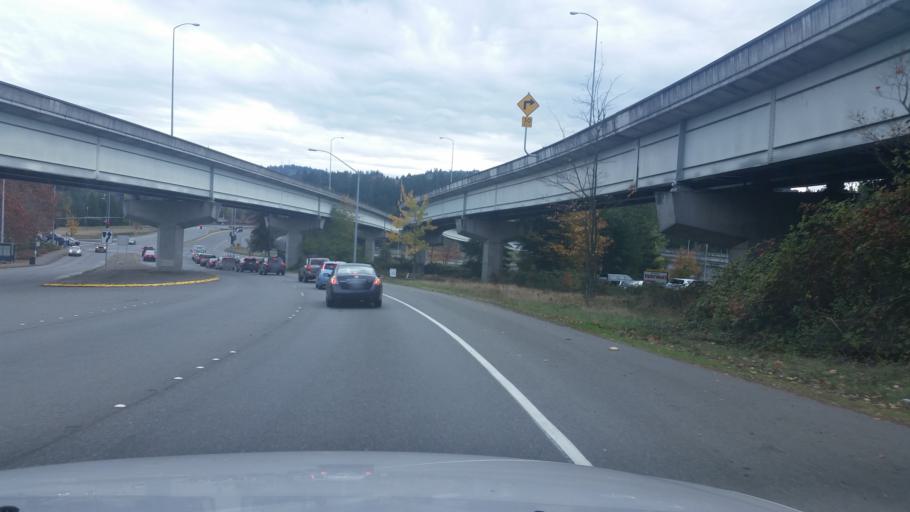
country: US
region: Washington
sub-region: King County
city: Eastgate
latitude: 47.5820
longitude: -122.1428
